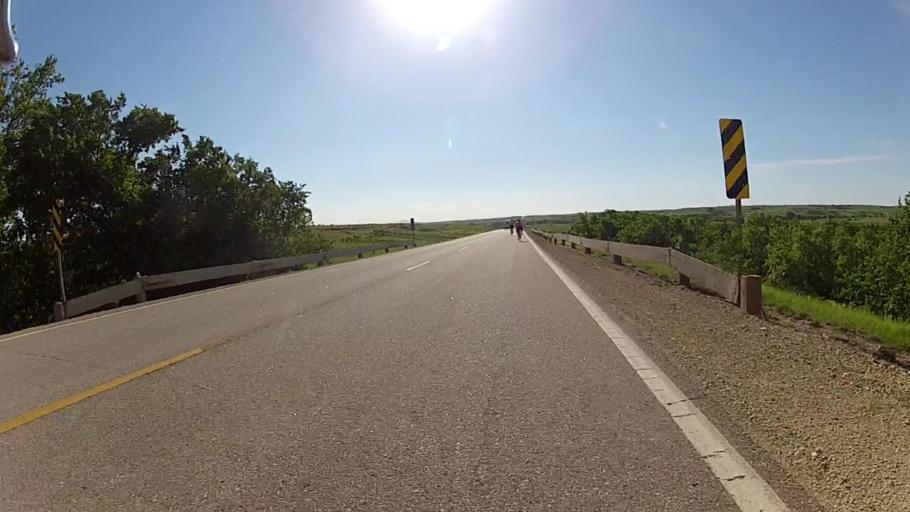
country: US
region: Kansas
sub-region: Barber County
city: Medicine Lodge
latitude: 37.2816
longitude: -98.8858
